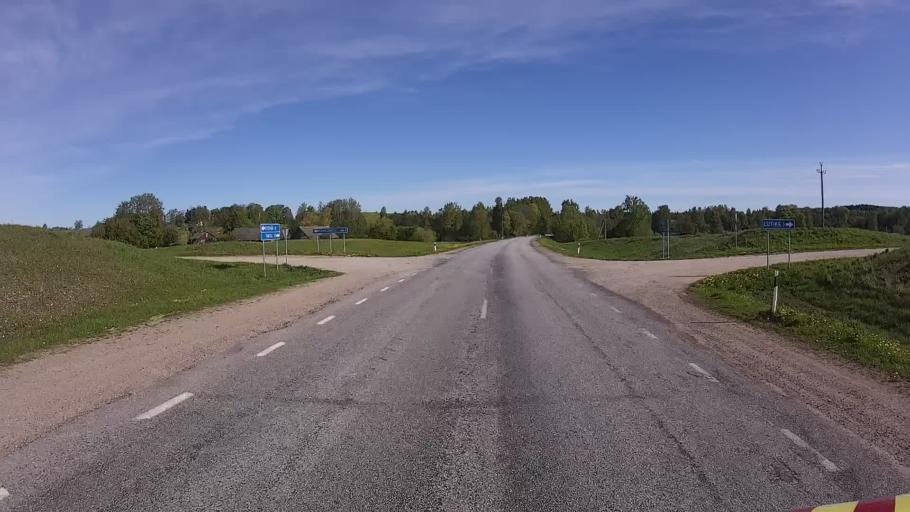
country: EE
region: Tartu
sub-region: Elva linn
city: Elva
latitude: 58.1365
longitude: 26.5206
